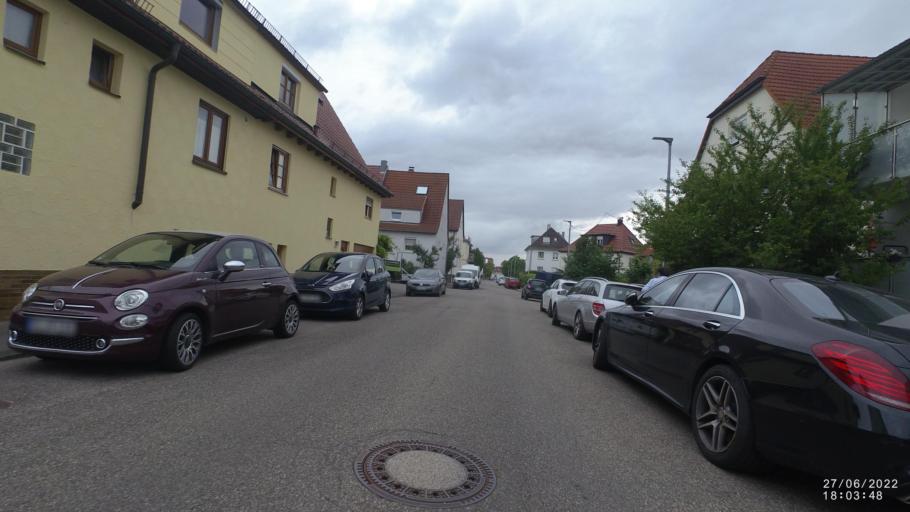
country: DE
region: Baden-Wuerttemberg
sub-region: Regierungsbezirk Stuttgart
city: Fellbach
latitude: 48.8029
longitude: 9.2803
